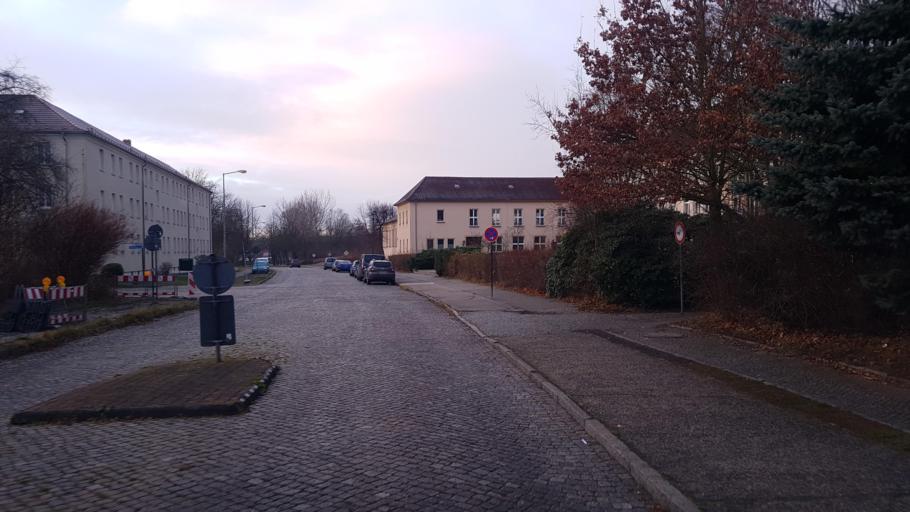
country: DE
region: Brandenburg
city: Lauchhammer
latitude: 51.4988
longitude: 13.7460
